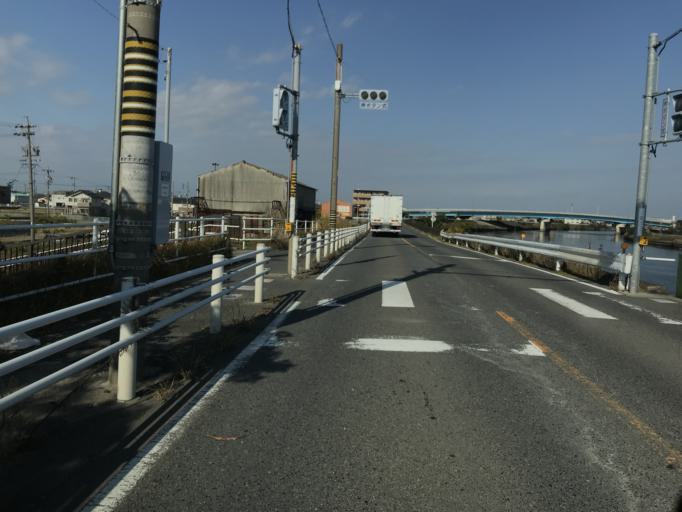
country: JP
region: Aichi
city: Kanie
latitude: 35.1660
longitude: 136.8263
